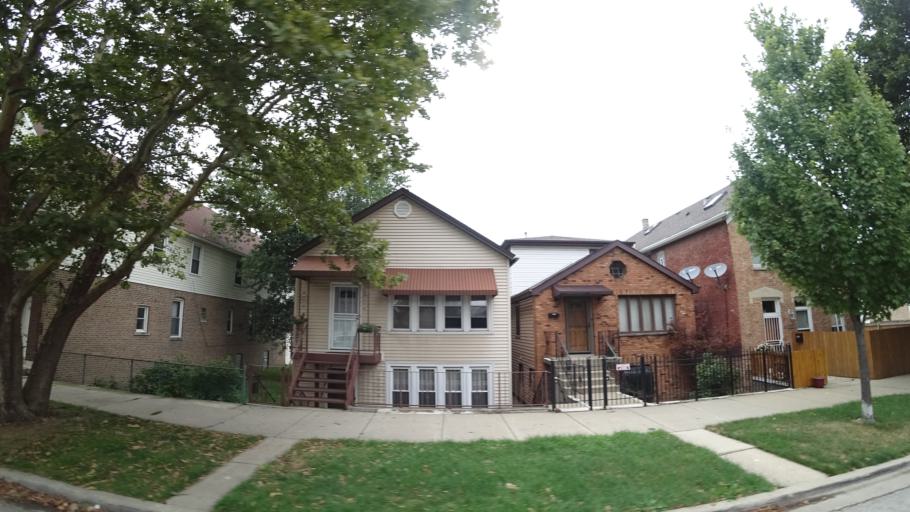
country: US
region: Illinois
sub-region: Cook County
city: Chicago
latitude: 41.8430
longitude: -87.6612
